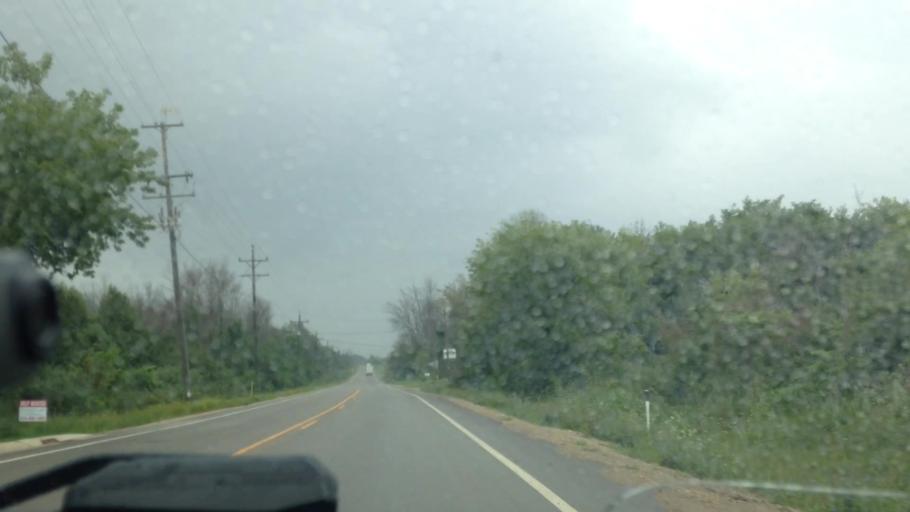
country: US
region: Wisconsin
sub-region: Washington County
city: Richfield
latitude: 43.2912
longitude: -88.2184
